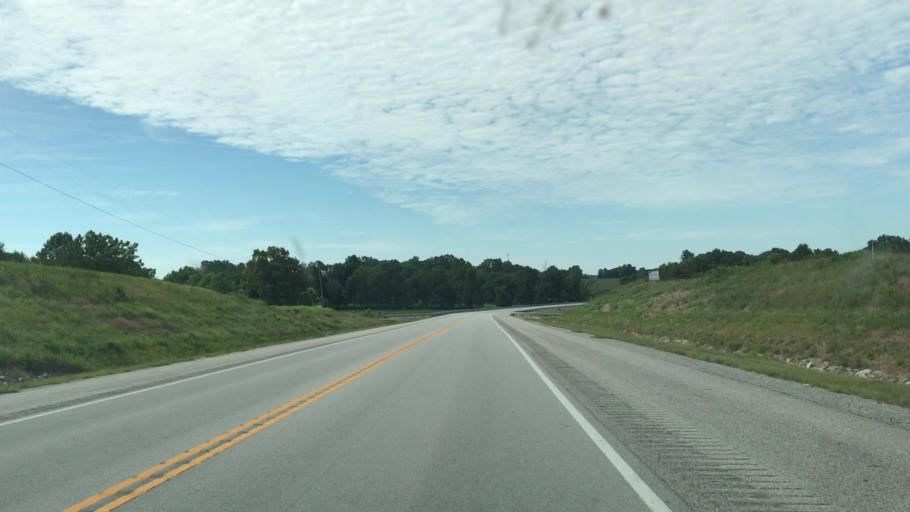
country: US
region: Kentucky
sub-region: Edmonson County
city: Brownsville
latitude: 37.1517
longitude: -86.2212
